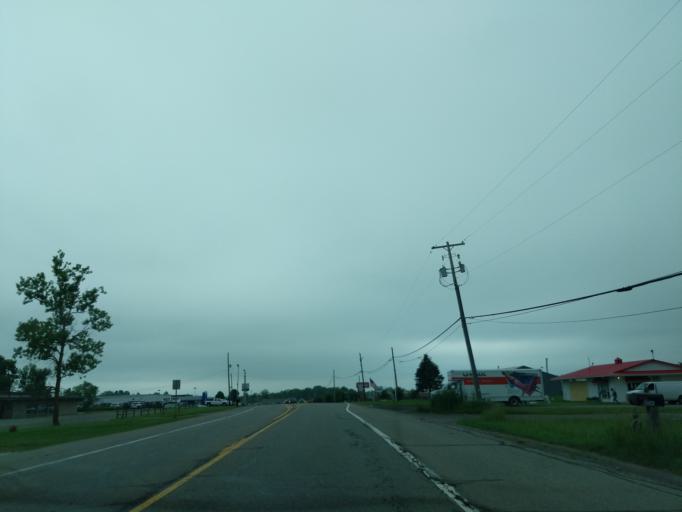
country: US
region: Michigan
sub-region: Branch County
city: Coldwater
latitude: 41.9365
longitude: -84.9549
